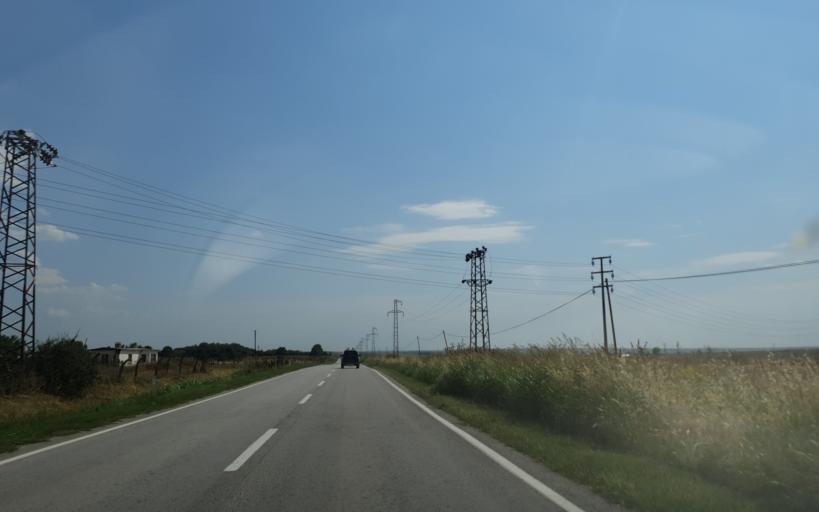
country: TR
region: Kirklareli
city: Buyukkaristiran
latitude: 41.3163
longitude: 27.5203
